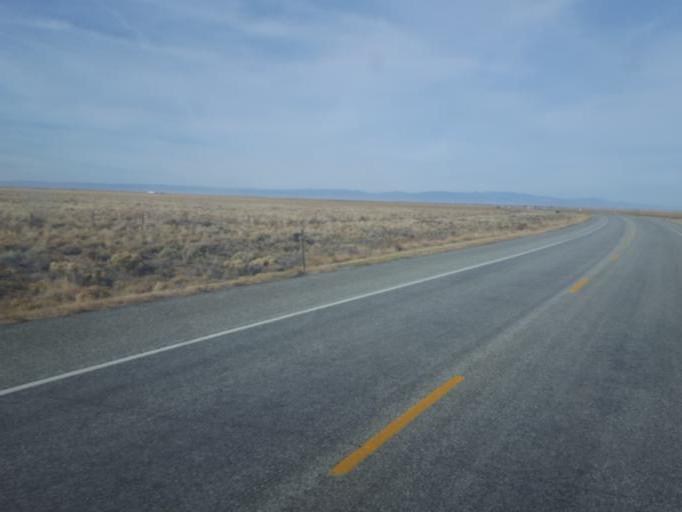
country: US
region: Colorado
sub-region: Alamosa County
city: Alamosa East
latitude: 37.4743
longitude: -105.5846
